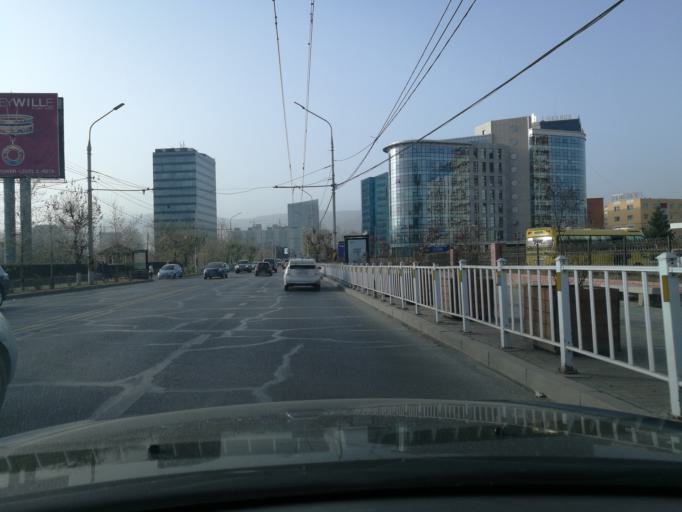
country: MN
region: Ulaanbaatar
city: Ulaanbaatar
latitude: 47.9127
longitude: 106.9149
